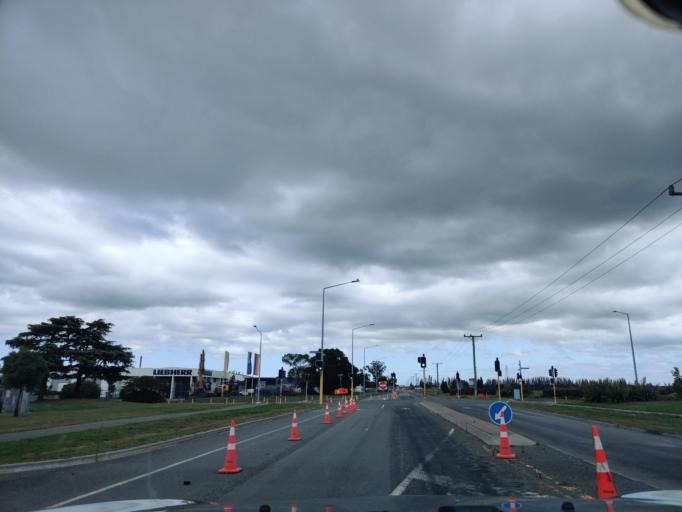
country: NZ
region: Canterbury
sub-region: Selwyn District
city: Prebbleton
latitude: -43.5551
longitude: 172.5127
